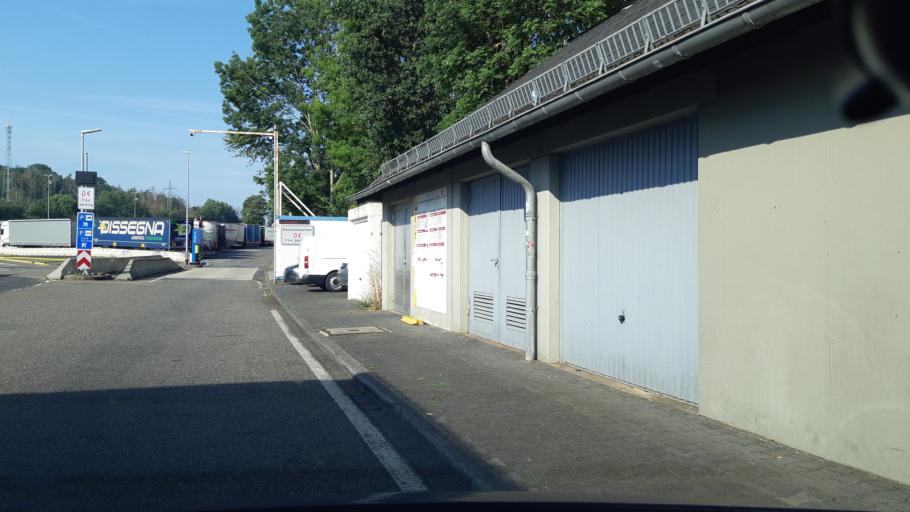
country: DE
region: Rheinland-Pfalz
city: Heiligenroth
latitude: 50.4482
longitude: 7.8509
